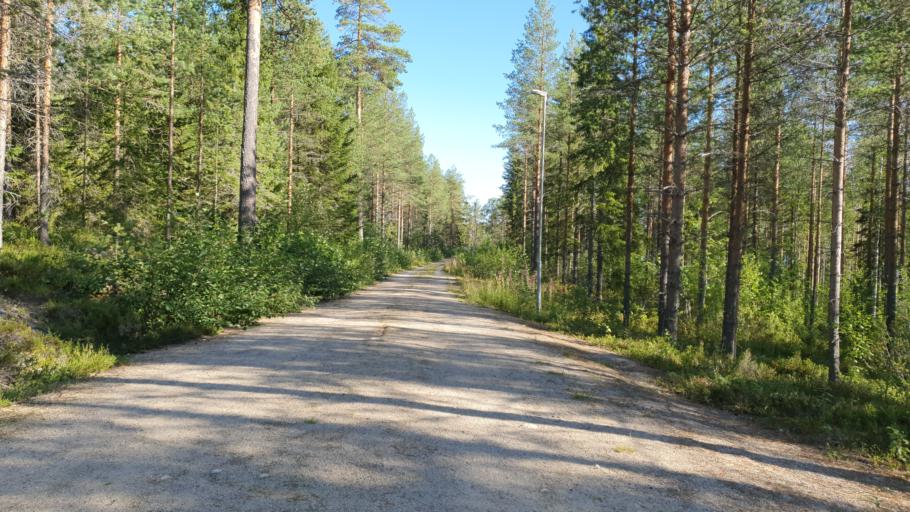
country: FI
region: Kainuu
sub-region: Kehys-Kainuu
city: Kuhmo
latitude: 64.1093
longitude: 29.5044
